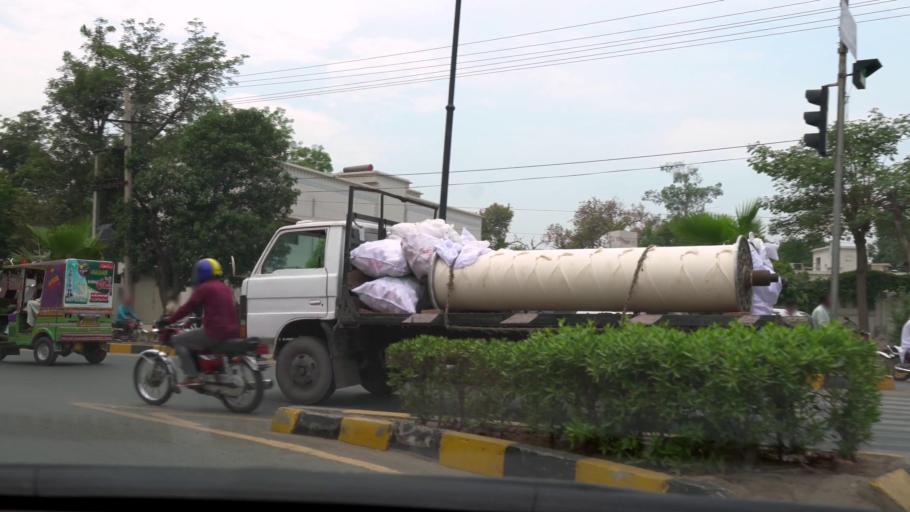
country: PK
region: Punjab
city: Faisalabad
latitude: 31.4295
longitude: 73.0844
